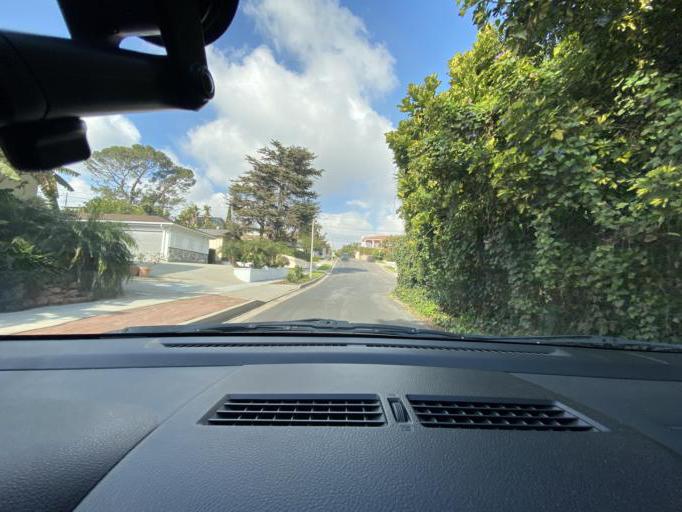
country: US
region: California
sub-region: Los Angeles County
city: Culver City
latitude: 34.0173
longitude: -118.4174
